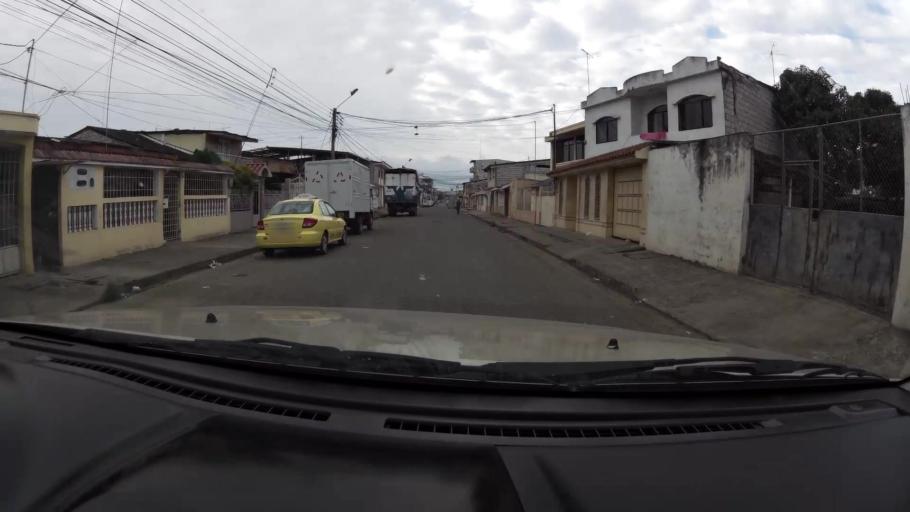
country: EC
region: El Oro
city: Machala
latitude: -3.2621
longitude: -79.9480
